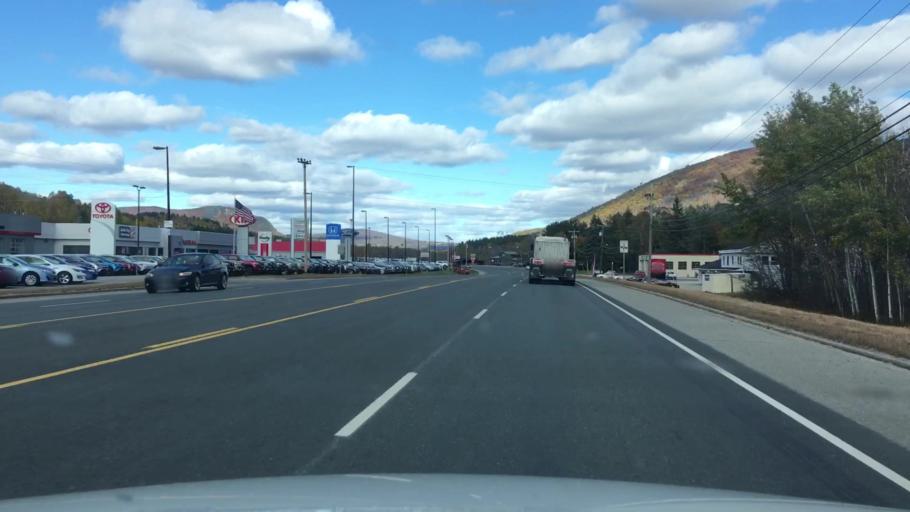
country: US
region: New Hampshire
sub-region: Coos County
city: Gorham
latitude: 44.4123
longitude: -71.1950
